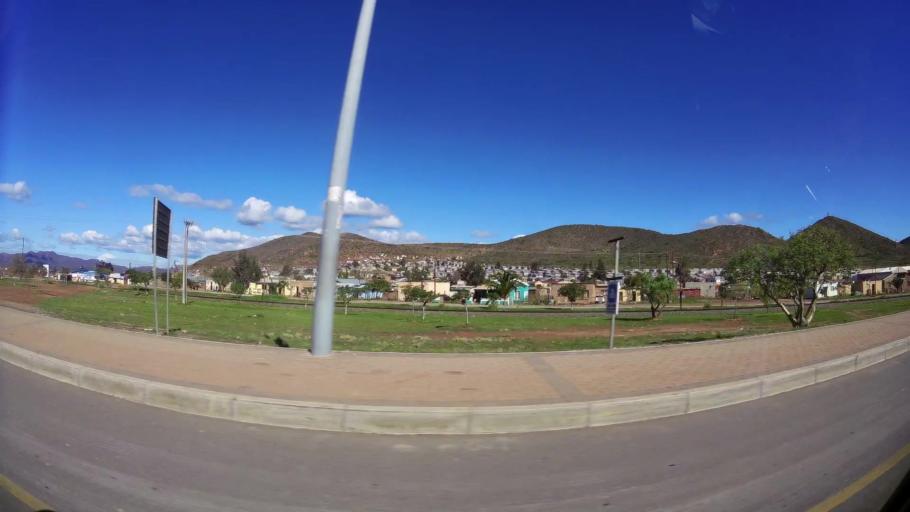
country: ZA
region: Western Cape
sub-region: Cape Winelands District Municipality
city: Ashton
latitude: -33.8147
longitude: 19.8923
